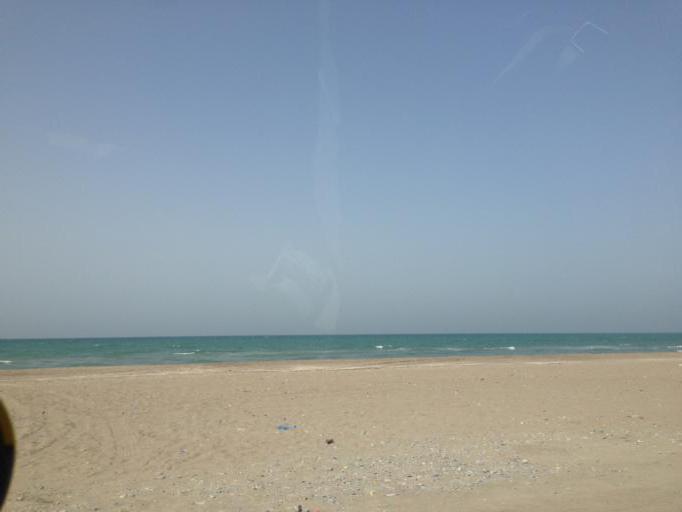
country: OM
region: Al Batinah
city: Barka'
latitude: 23.7121
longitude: 57.8791
